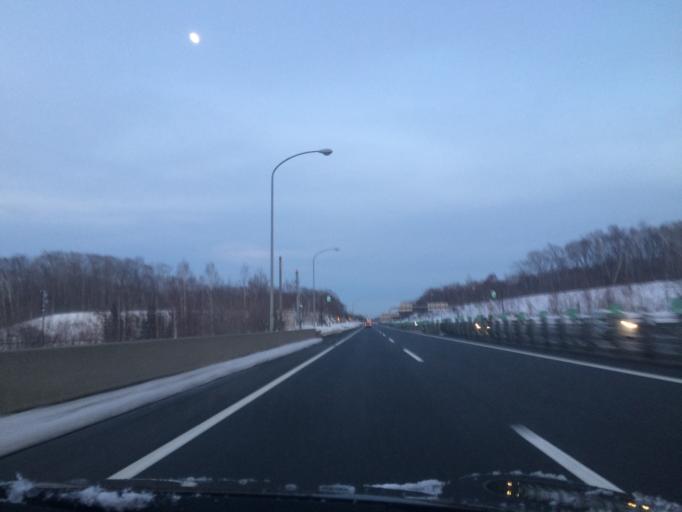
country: JP
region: Hokkaido
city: Chitose
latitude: 42.8451
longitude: 141.5859
